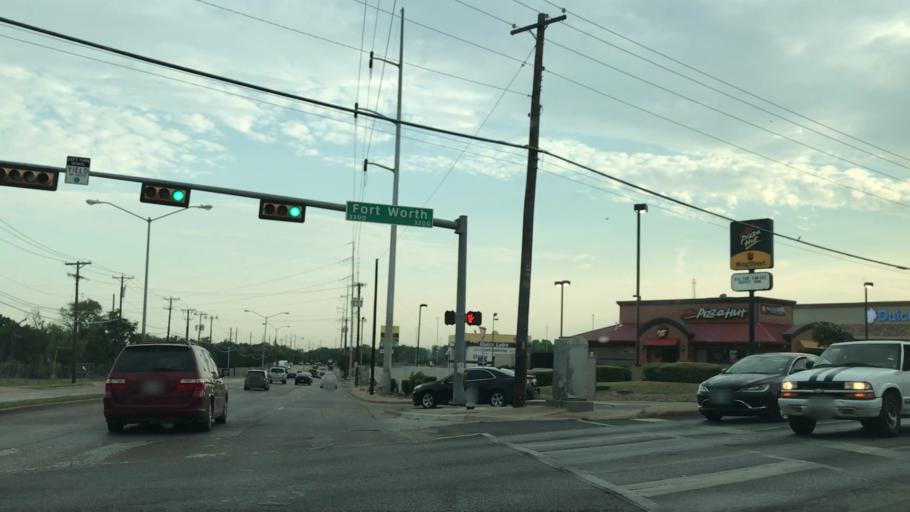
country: US
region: Texas
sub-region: Dallas County
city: Cockrell Hill
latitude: 32.7536
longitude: -96.8740
